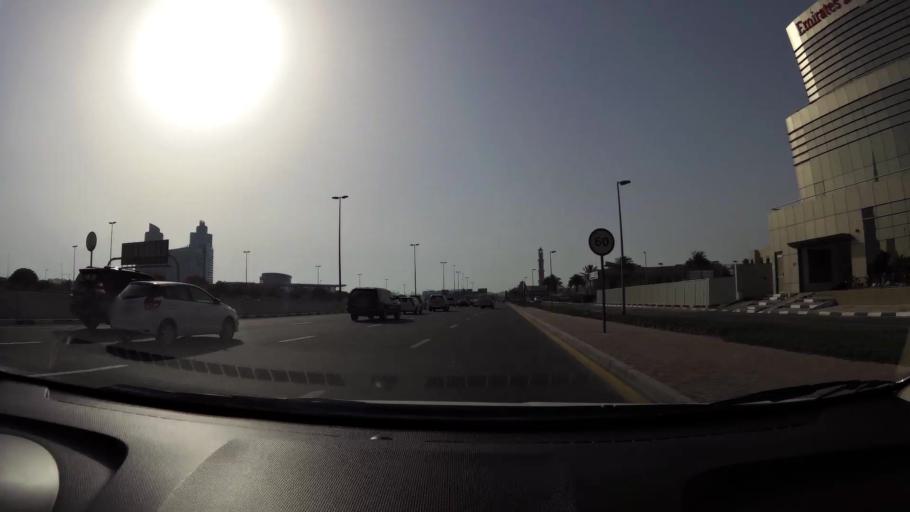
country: AE
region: Ash Shariqah
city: Sharjah
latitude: 25.2307
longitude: 55.3530
